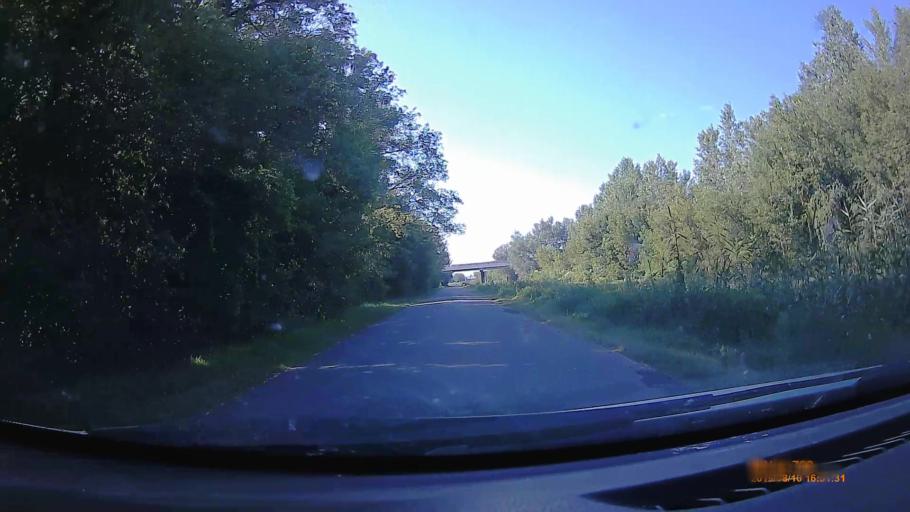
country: HU
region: Somogy
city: Balatonfenyves
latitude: 46.7011
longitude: 17.4853
